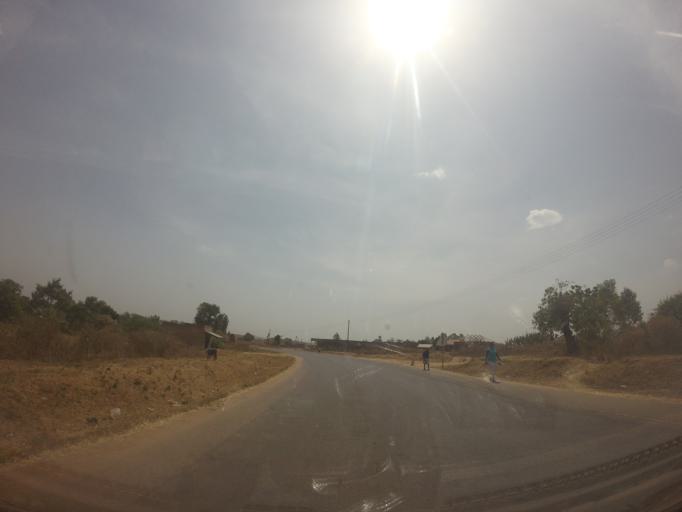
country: UG
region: Northern Region
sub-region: Arua District
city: Arua
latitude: 2.9546
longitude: 30.9177
